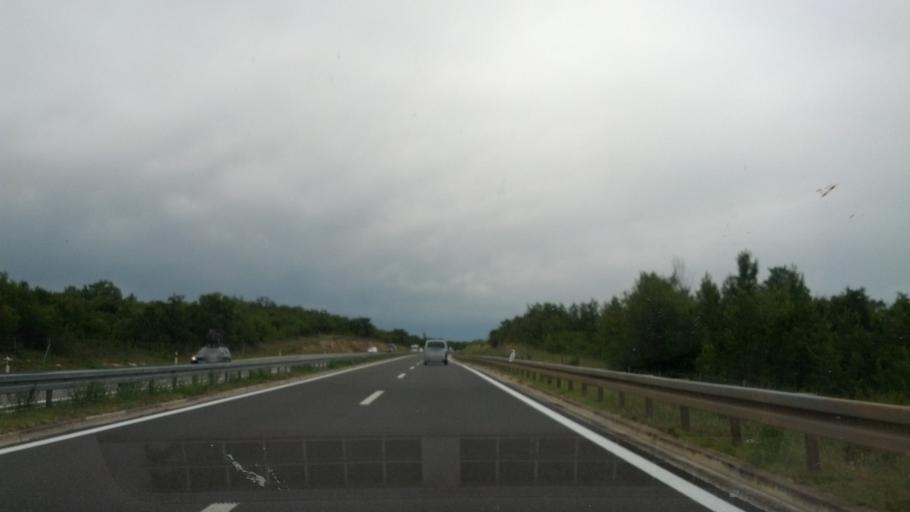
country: HR
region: Istarska
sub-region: Grad Rovinj
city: Rovinj
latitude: 45.1410
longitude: 13.7565
